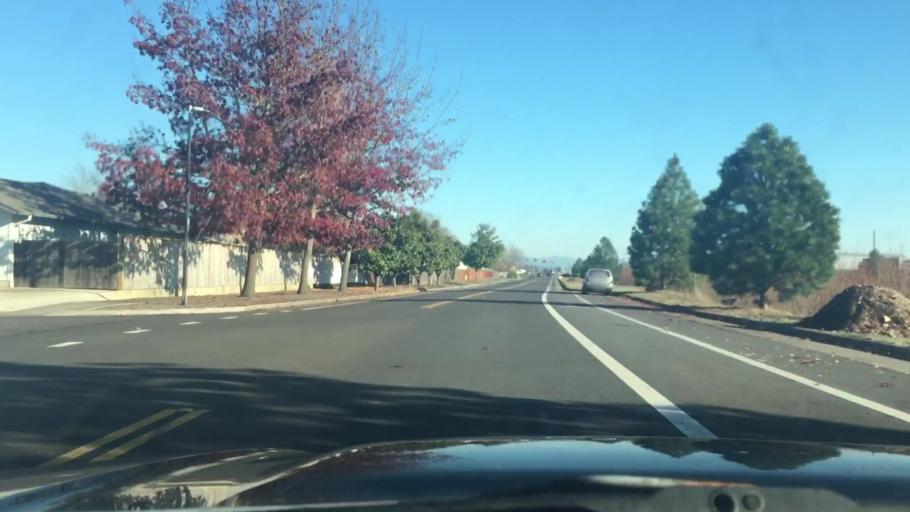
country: US
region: Oregon
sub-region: Lane County
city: Eugene
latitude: 44.0647
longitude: -123.1828
